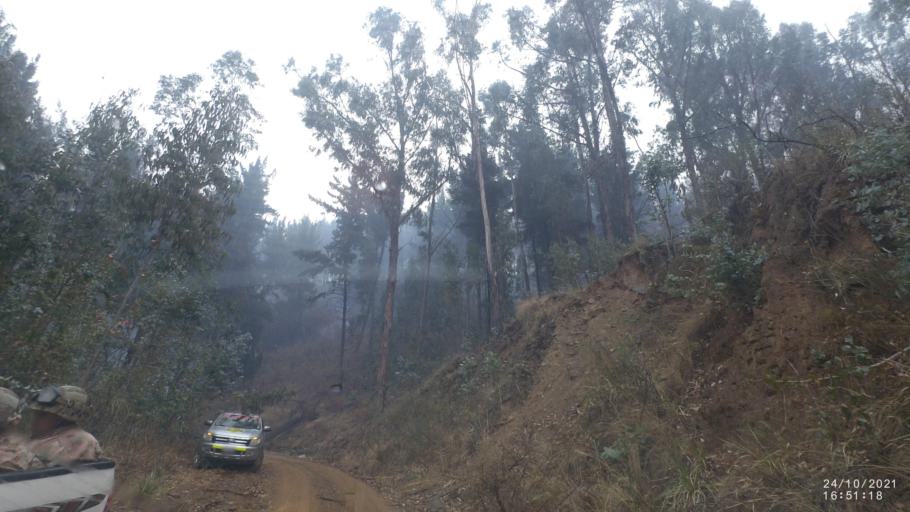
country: BO
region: Cochabamba
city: Cochabamba
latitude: -17.3391
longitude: -66.1413
